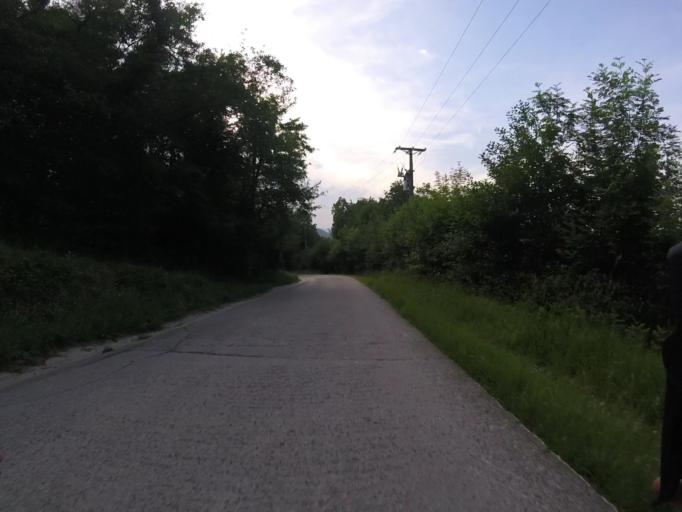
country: ES
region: Basque Country
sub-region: Provincia de Guipuzcoa
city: Errenteria
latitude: 43.2655
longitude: -1.8936
